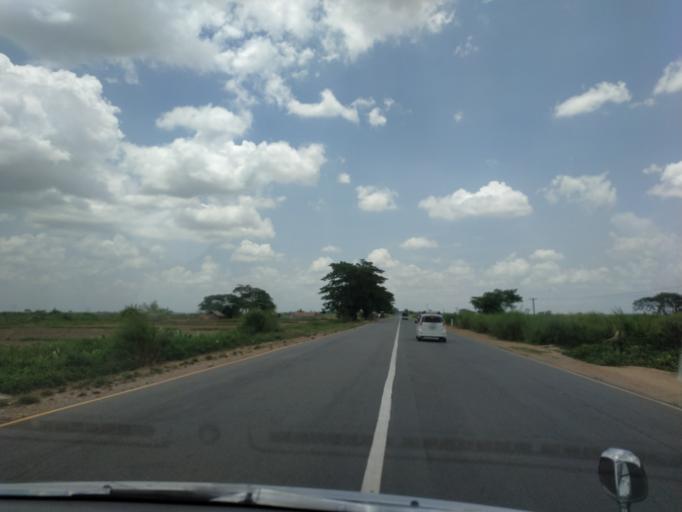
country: MM
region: Bago
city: Bago
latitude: 17.4700
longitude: 96.5589
